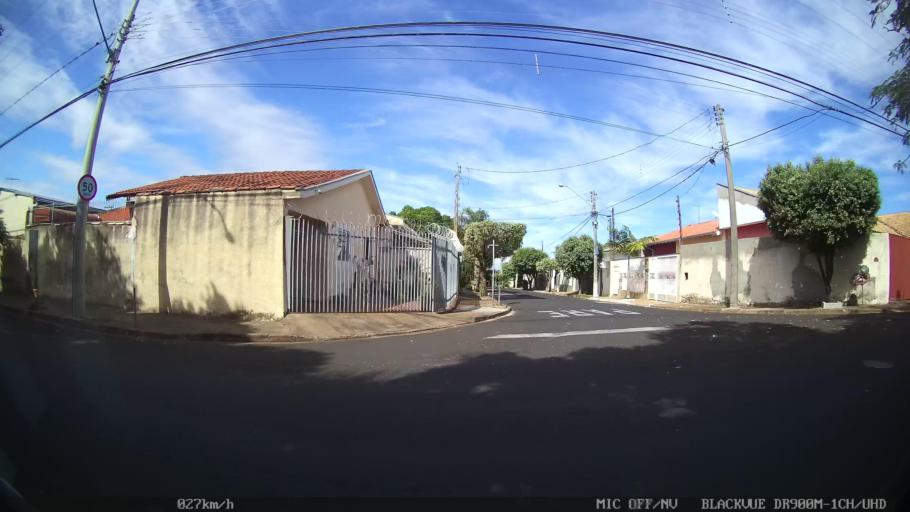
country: BR
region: Sao Paulo
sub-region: Sao Jose Do Rio Preto
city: Sao Jose do Rio Preto
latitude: -20.8333
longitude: -49.3534
